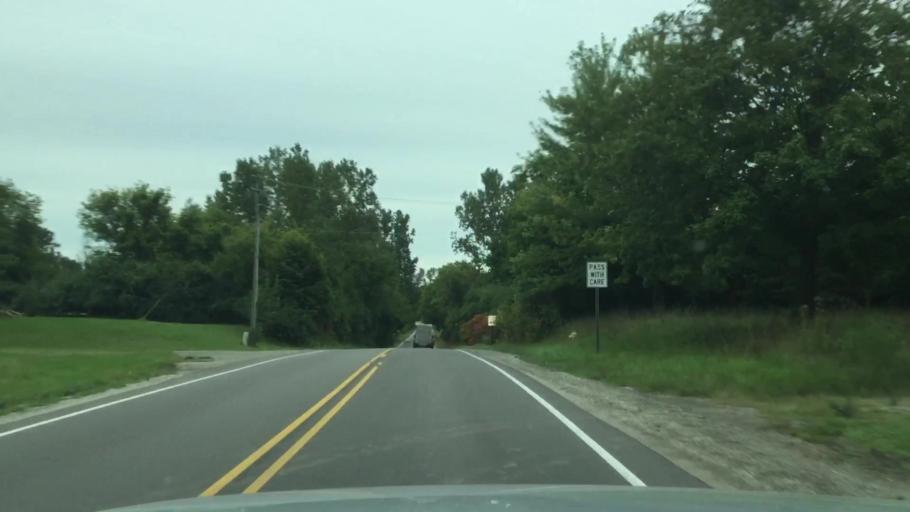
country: US
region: Michigan
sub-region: Washtenaw County
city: Ypsilanti
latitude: 42.2041
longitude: -83.6209
